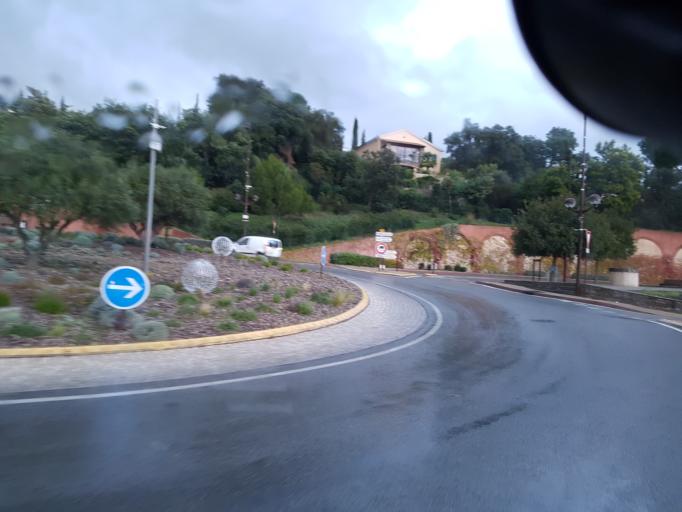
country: FR
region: Provence-Alpes-Cote d'Azur
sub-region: Departement du Var
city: La Croix-Valmer
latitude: 43.2053
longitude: 6.5682
